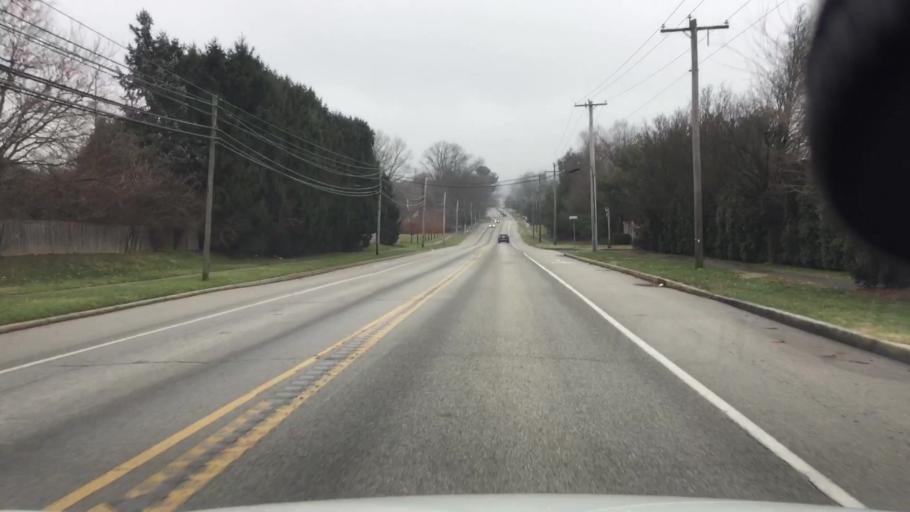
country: US
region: Pennsylvania
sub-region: Montgomery County
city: Fort Washington
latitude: 40.1554
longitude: -75.1908
